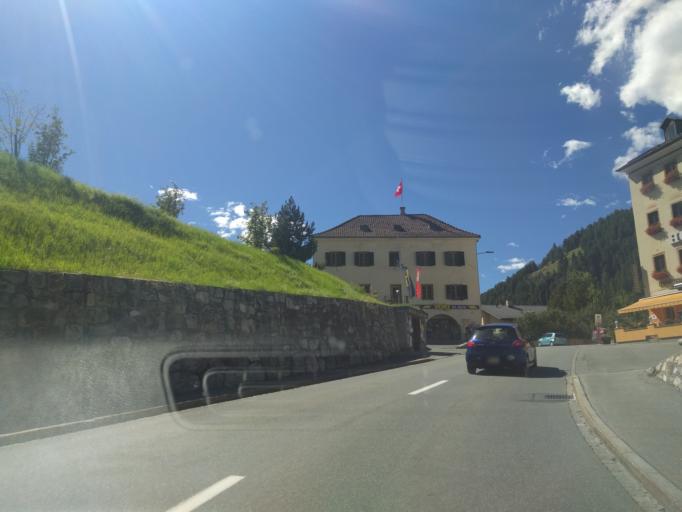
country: IT
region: Trentino-Alto Adige
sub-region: Bolzano
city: Tubre
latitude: 46.6009
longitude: 10.4230
